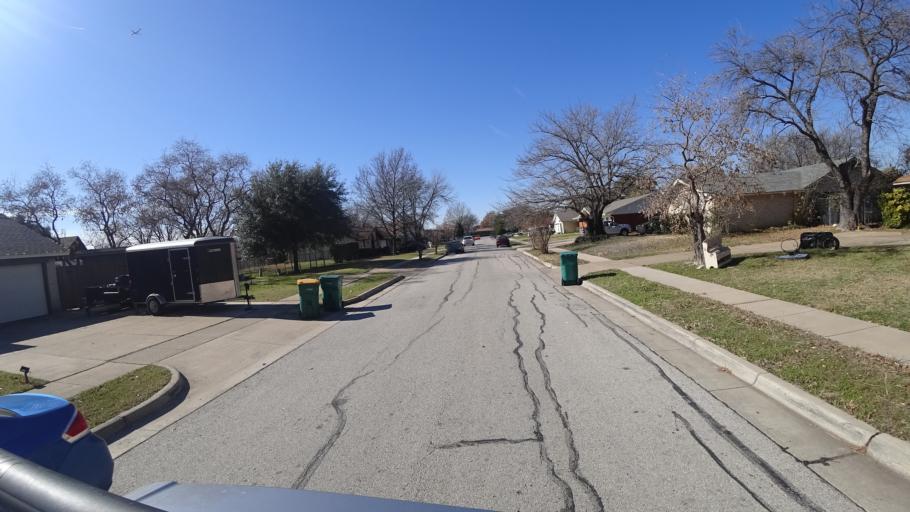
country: US
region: Texas
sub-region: Denton County
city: Lewisville
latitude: 33.0330
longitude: -97.0170
